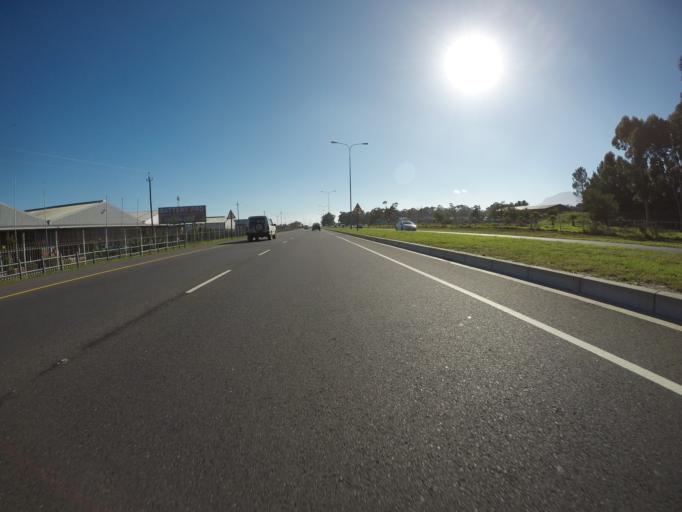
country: ZA
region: Western Cape
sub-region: Overberg District Municipality
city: Grabouw
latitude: -34.1199
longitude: 18.8803
